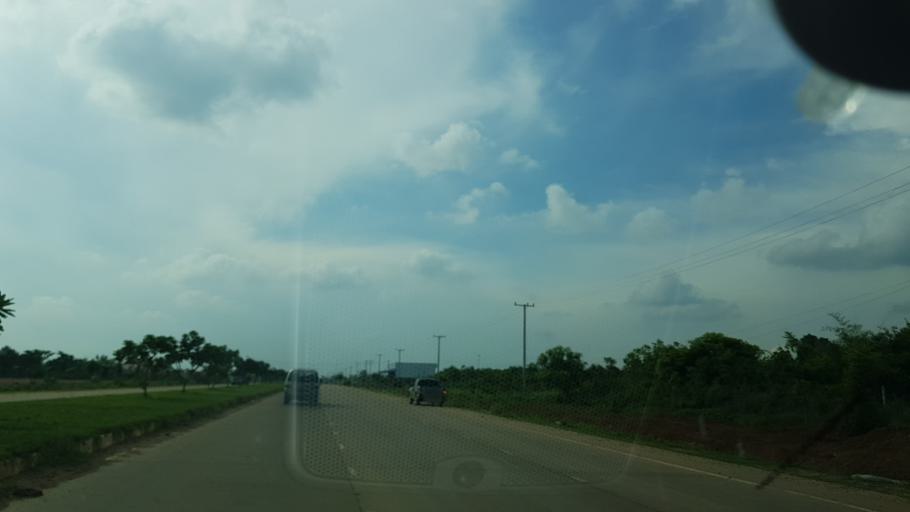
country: LA
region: Vientiane
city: Vientiane
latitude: 17.9941
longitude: 102.7113
